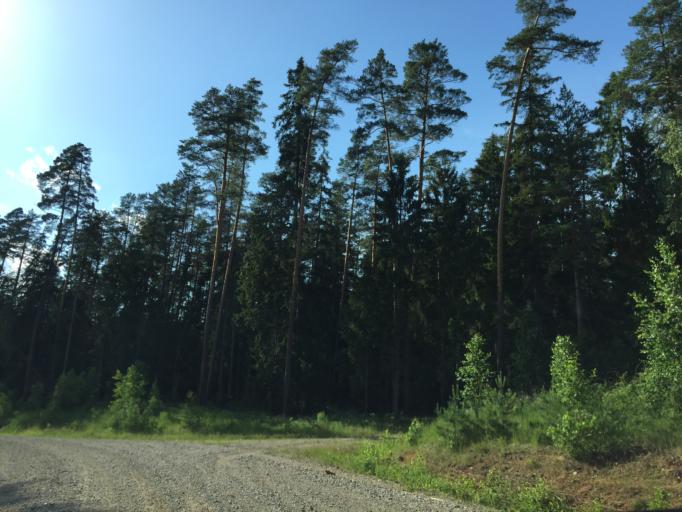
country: LV
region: Tukuma Rajons
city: Tukums
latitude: 57.0328
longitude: 23.2143
